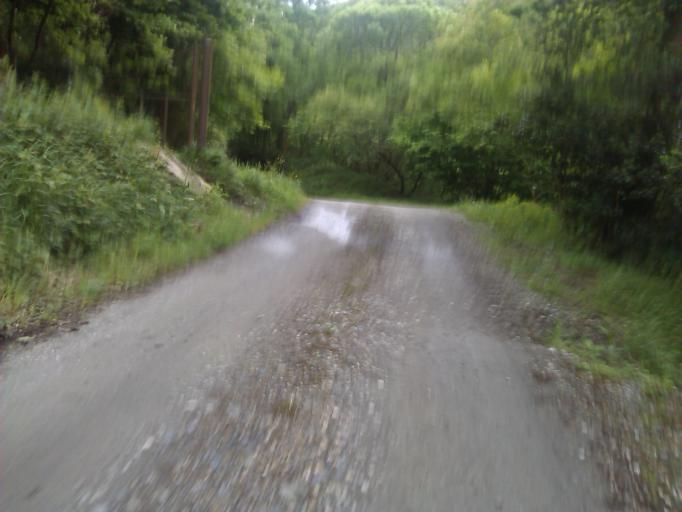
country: ES
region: Basque Country
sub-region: Provincia de Guipuzcoa
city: Berastegui
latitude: 43.1289
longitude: -1.9389
